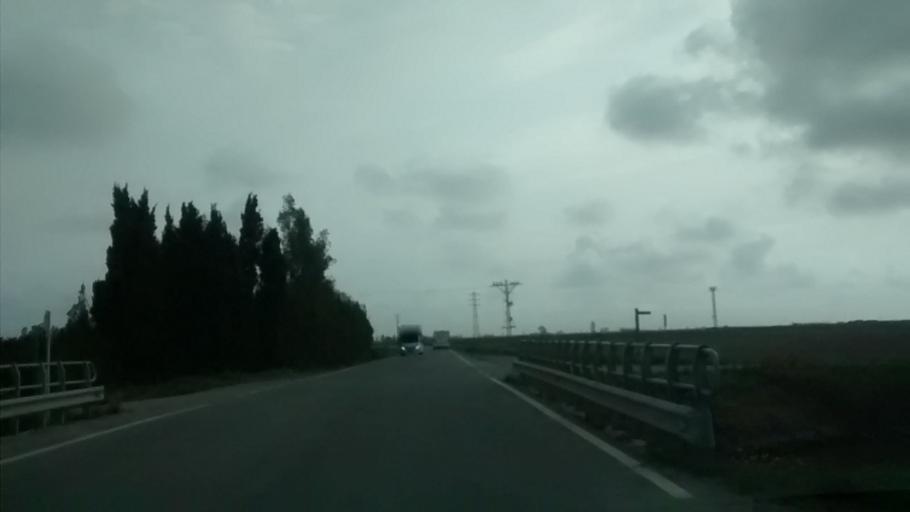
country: ES
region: Catalonia
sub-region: Provincia de Tarragona
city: Sant Carles de la Rapita
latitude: 40.6537
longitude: 0.6268
